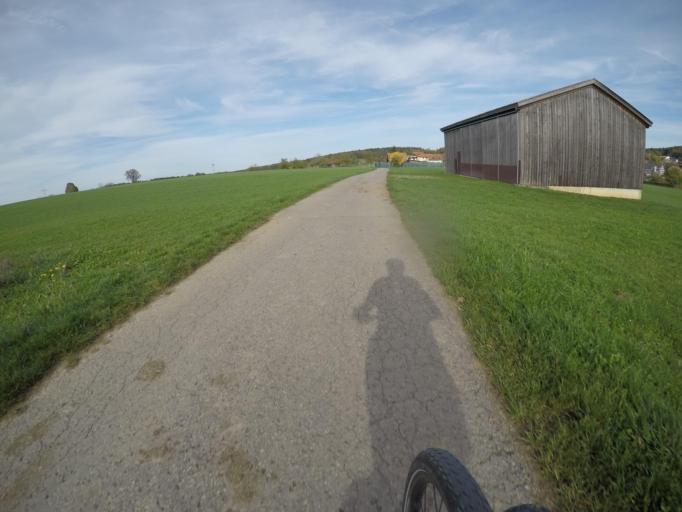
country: DE
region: Baden-Wuerttemberg
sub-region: Karlsruhe Region
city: Simmozheim
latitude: 48.7621
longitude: 8.7941
